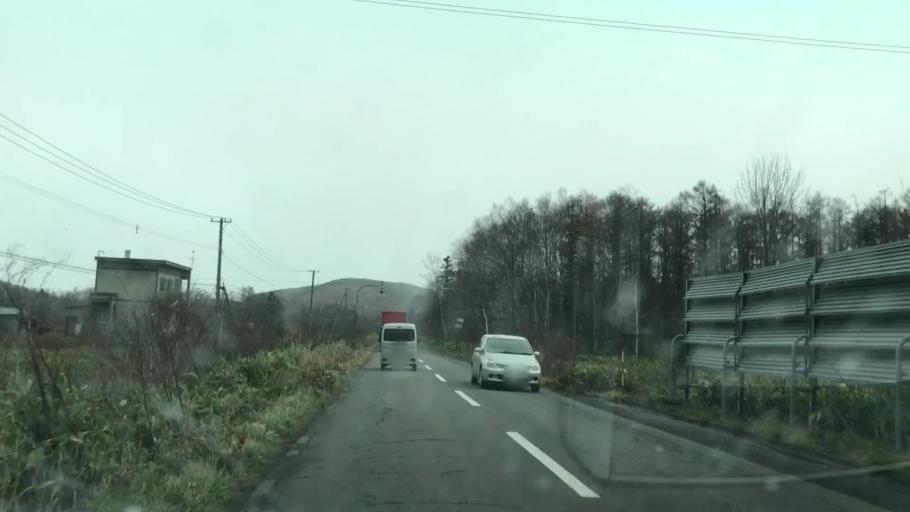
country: JP
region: Hokkaido
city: Yoichi
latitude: 43.3165
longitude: 140.5353
